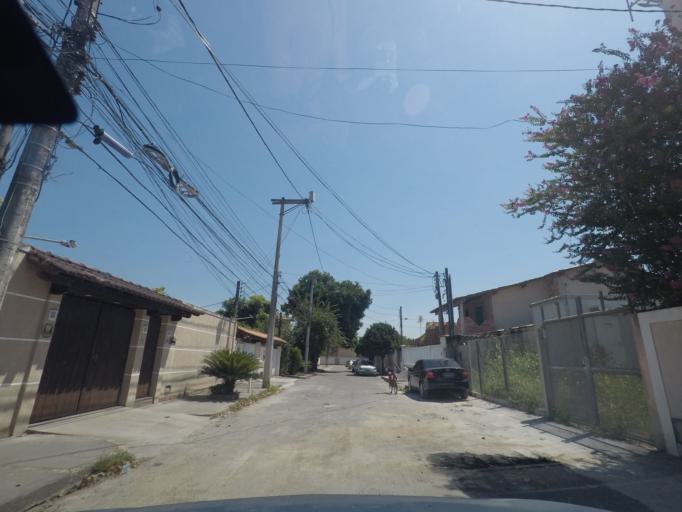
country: BR
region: Rio de Janeiro
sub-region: Niteroi
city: Niteroi
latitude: -22.9398
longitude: -43.0224
